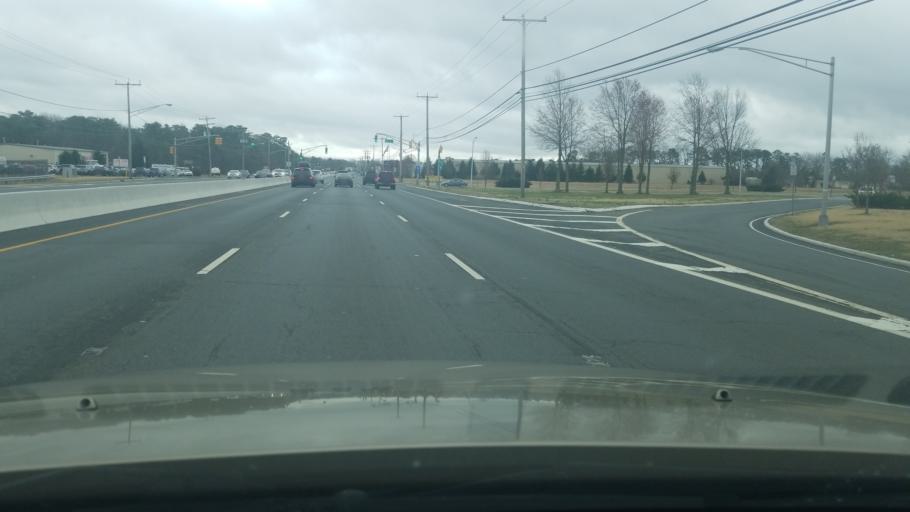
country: US
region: New Jersey
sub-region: Ocean County
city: Pine Lake Park
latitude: 39.9858
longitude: -74.2596
